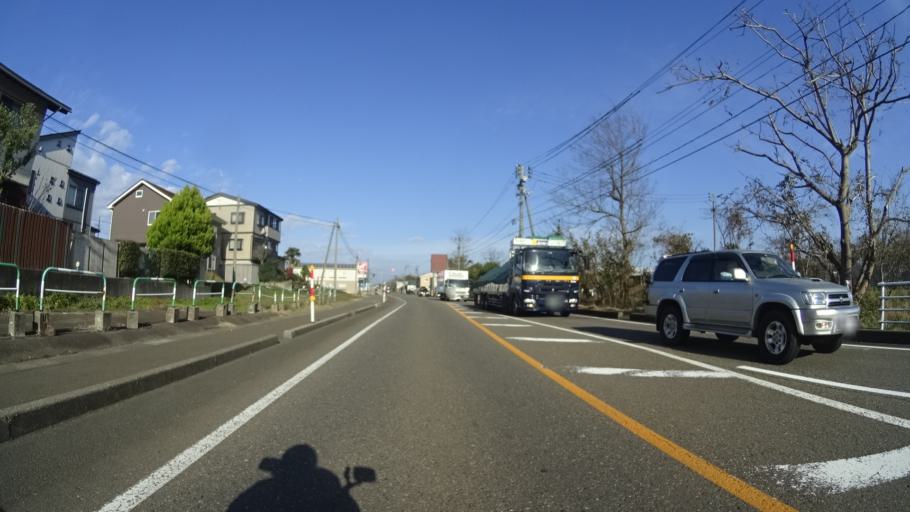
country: JP
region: Niigata
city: Joetsu
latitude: 37.2268
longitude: 138.3299
